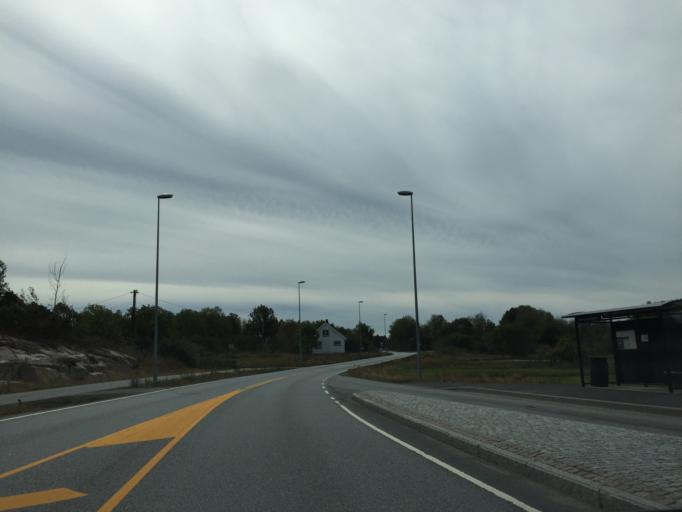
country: NO
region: Ostfold
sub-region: Hvaler
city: Skjaerhalden
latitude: 59.0747
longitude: 10.9380
